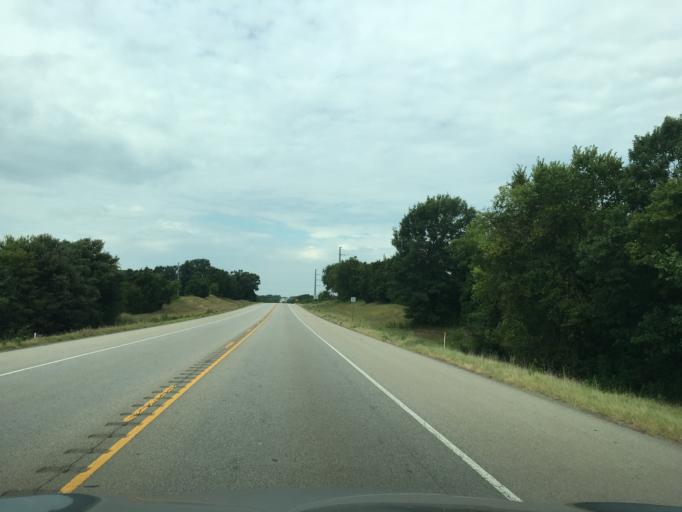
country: US
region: Texas
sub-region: Collin County
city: Anna
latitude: 33.3251
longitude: -96.4932
